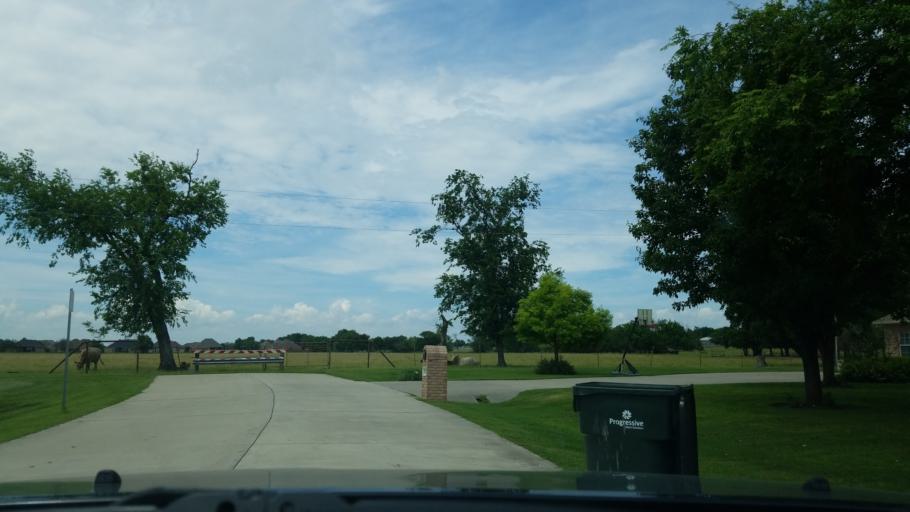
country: US
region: Texas
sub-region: Denton County
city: Sanger
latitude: 33.3601
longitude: -97.1930
